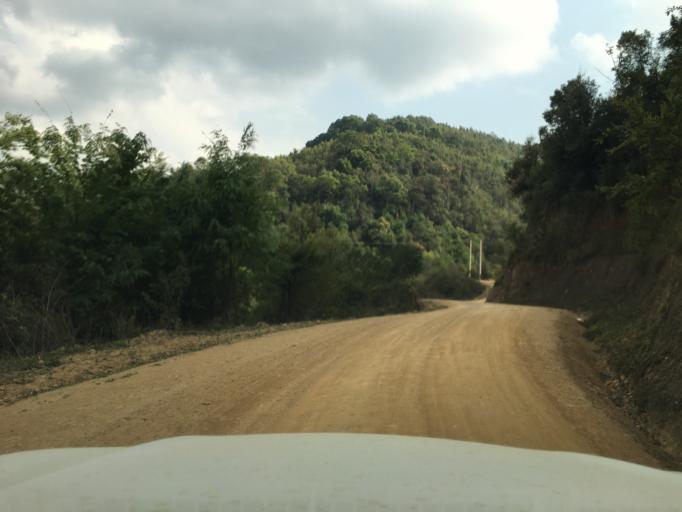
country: LA
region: Houaphan
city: Huameung
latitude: 20.2078
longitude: 103.8538
